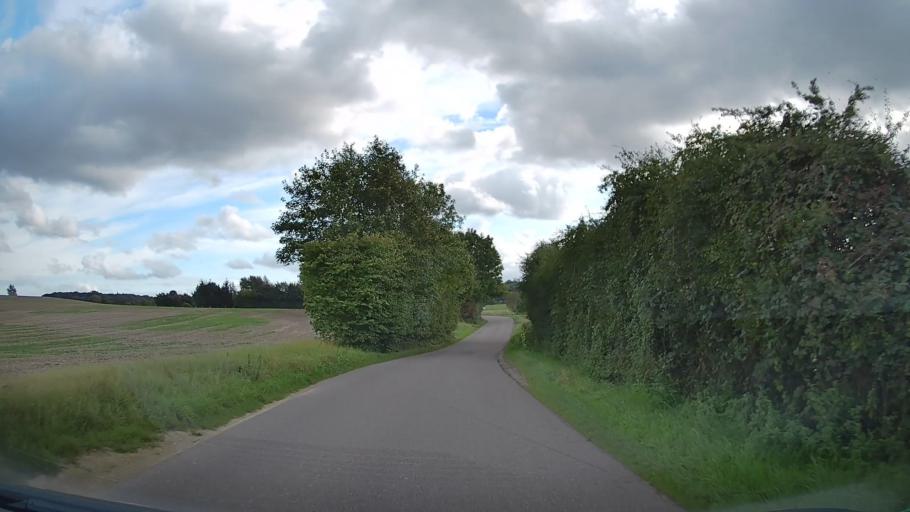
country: DE
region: Schleswig-Holstein
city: Steinberg
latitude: 54.7817
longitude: 9.7799
